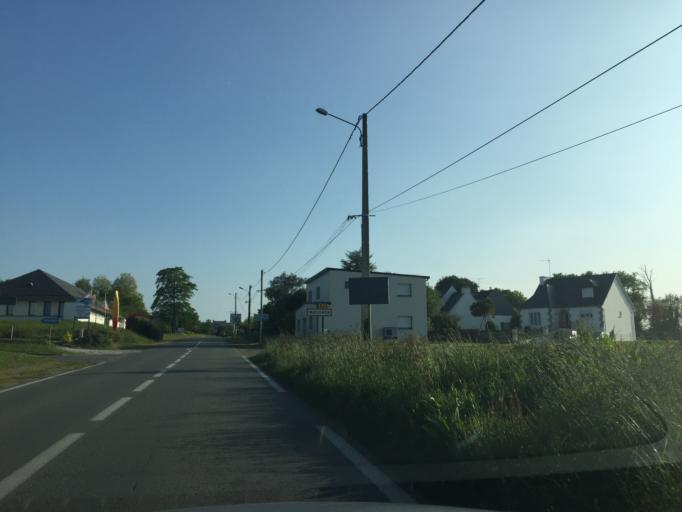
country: FR
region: Brittany
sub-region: Departement des Cotes-d'Armor
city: Matignon
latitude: 48.6019
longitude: -2.2861
